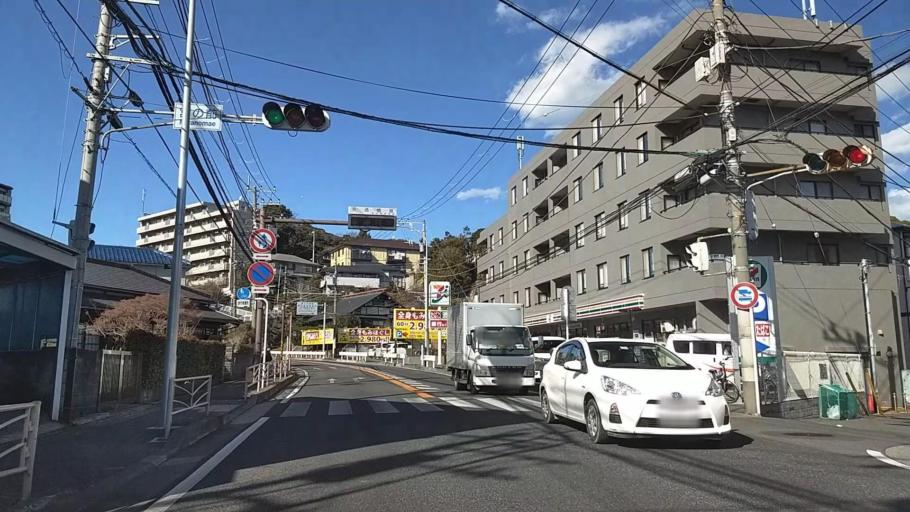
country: JP
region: Kanagawa
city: Yokohama
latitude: 35.3699
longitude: 139.6340
